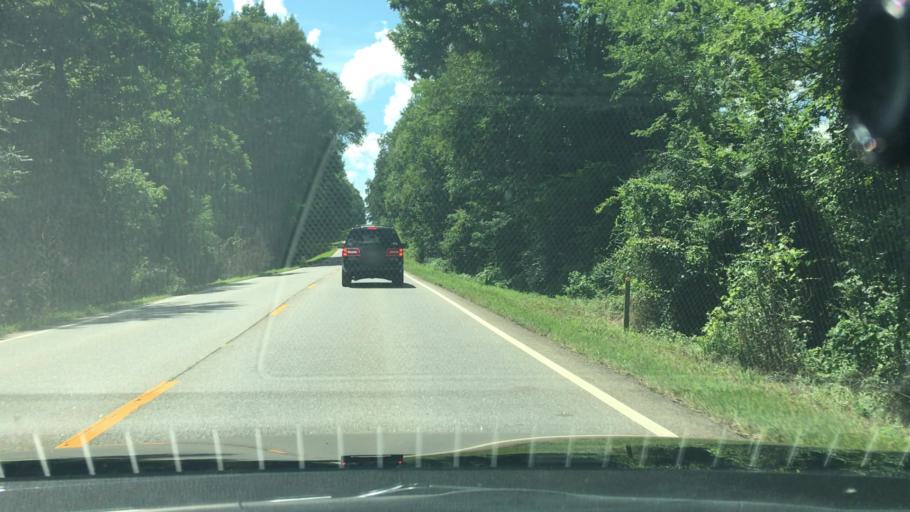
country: US
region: Georgia
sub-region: Putnam County
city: Eatonton
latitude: 33.3095
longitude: -83.5125
